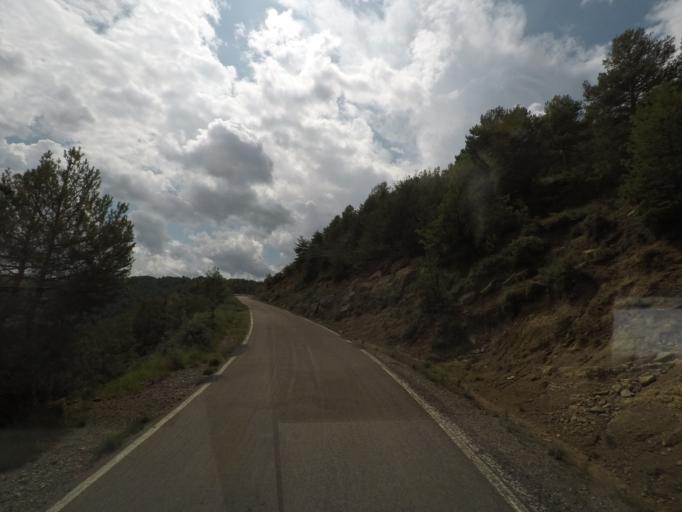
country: ES
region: Aragon
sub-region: Provincia de Huesca
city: Boltana
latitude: 42.4021
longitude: -0.0100
